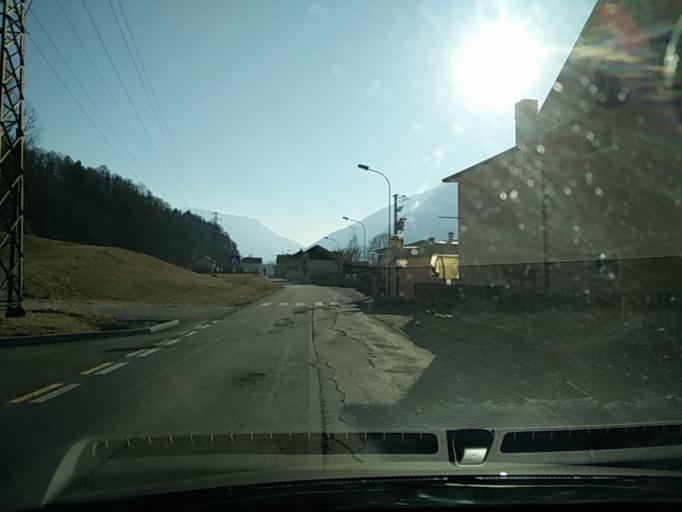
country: IT
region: Veneto
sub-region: Provincia di Belluno
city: Puos d'Alpago
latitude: 46.1429
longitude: 12.3297
